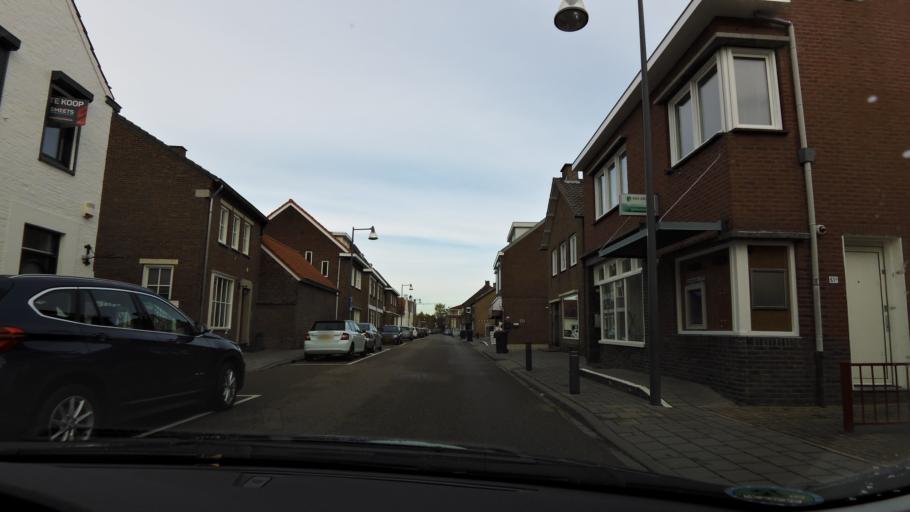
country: NL
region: Limburg
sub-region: Gemeente Sittard-Geleen
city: Born
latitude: 51.0428
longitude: 5.8083
